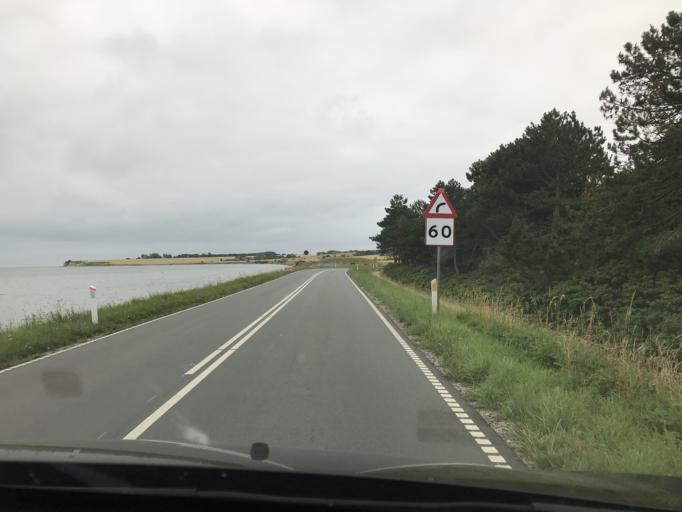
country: DK
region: South Denmark
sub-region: AEro Kommune
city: AEroskobing
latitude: 54.8375
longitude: 10.4508
